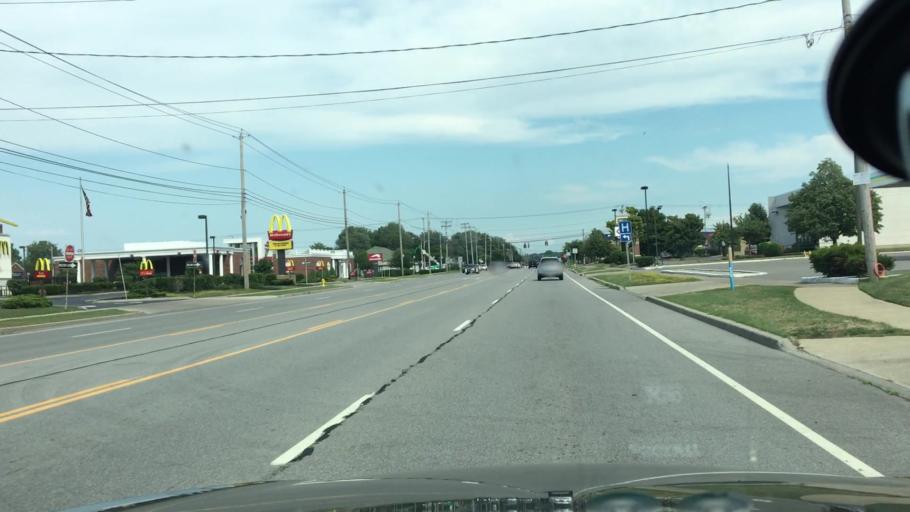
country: US
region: New York
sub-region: Erie County
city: Williamsville
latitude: 42.9785
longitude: -78.7423
